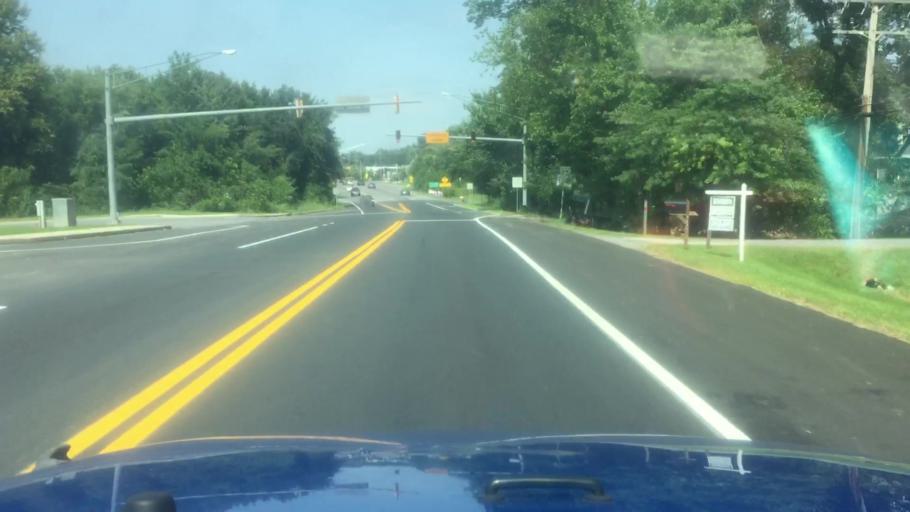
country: US
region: Maryland
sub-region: Anne Arundel County
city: Severn
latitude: 39.1338
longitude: -76.6874
